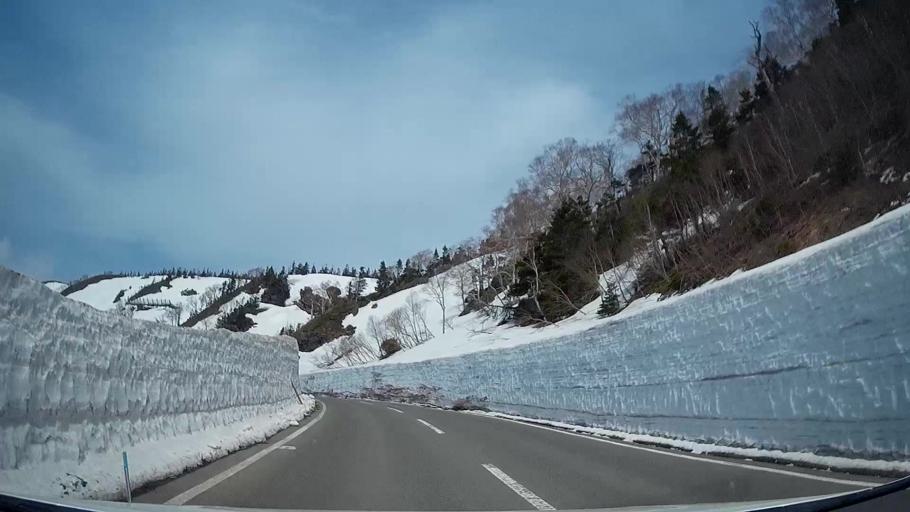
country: JP
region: Akita
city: Hanawa
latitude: 39.9516
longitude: 140.8709
